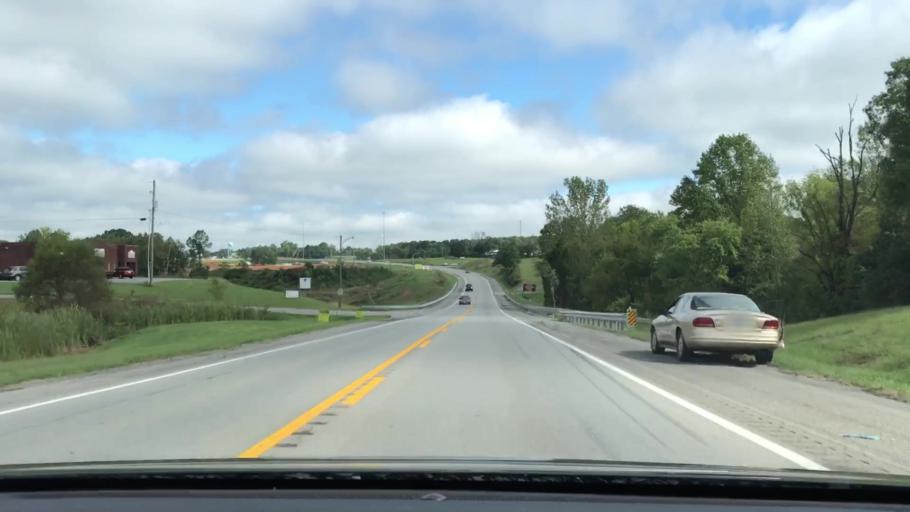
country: US
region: Kentucky
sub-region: Russell County
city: Russell Springs
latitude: 37.0416
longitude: -85.0729
